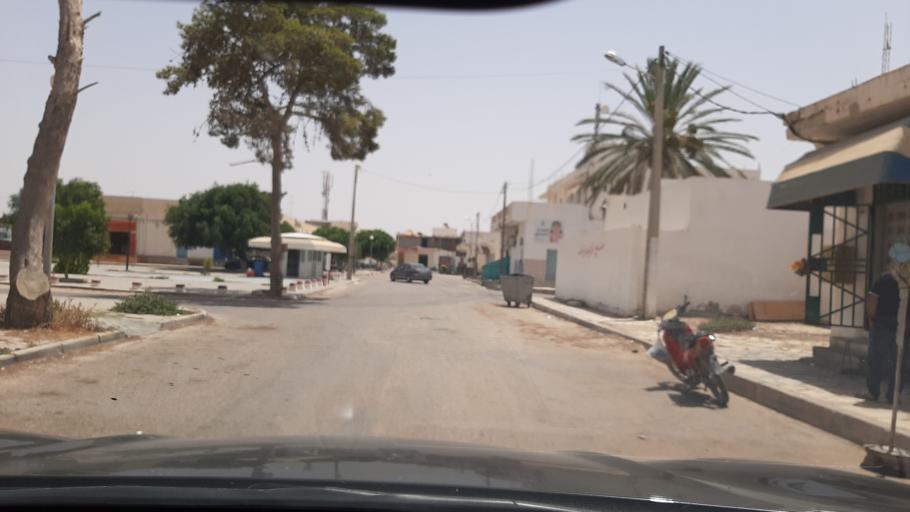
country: TN
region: Qabis
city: Matmata
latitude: 33.6177
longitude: 10.2883
